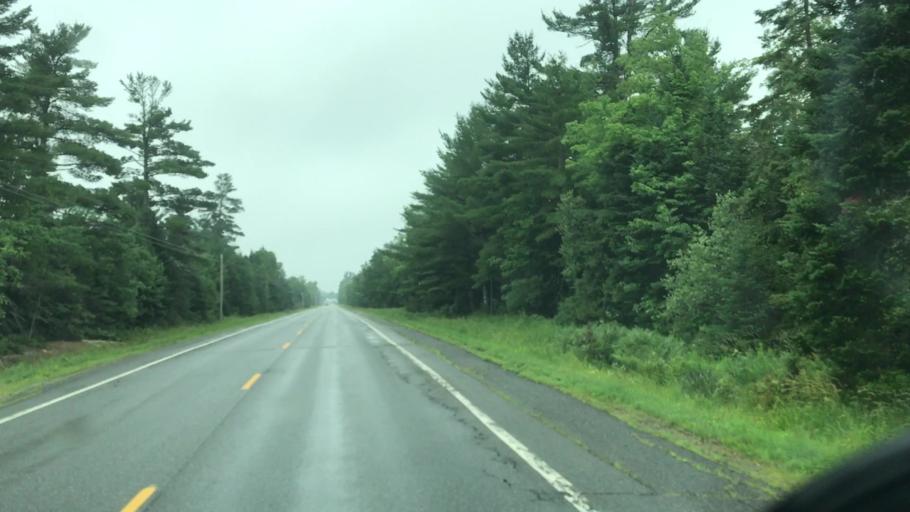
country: US
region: Maine
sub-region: Penobscot County
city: Enfield
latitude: 45.3071
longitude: -68.6112
